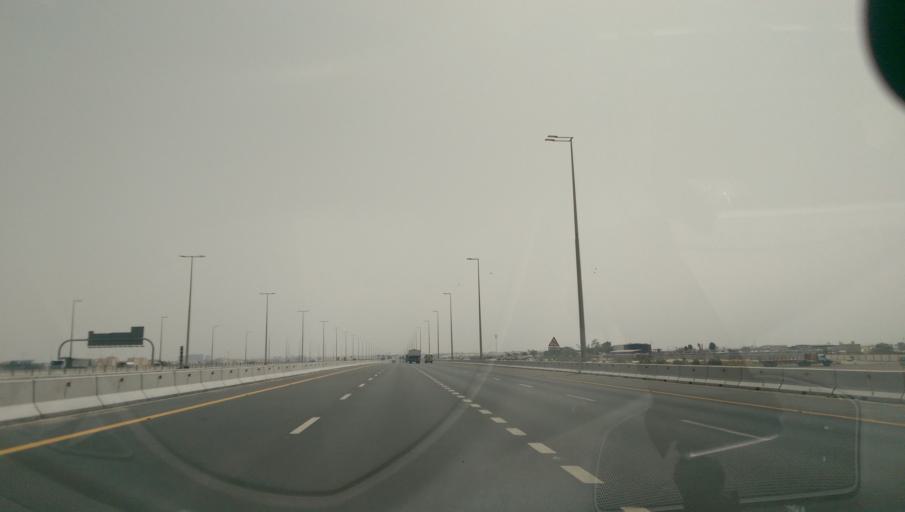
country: AE
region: Abu Dhabi
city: Abu Dhabi
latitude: 24.2923
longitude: 54.5668
